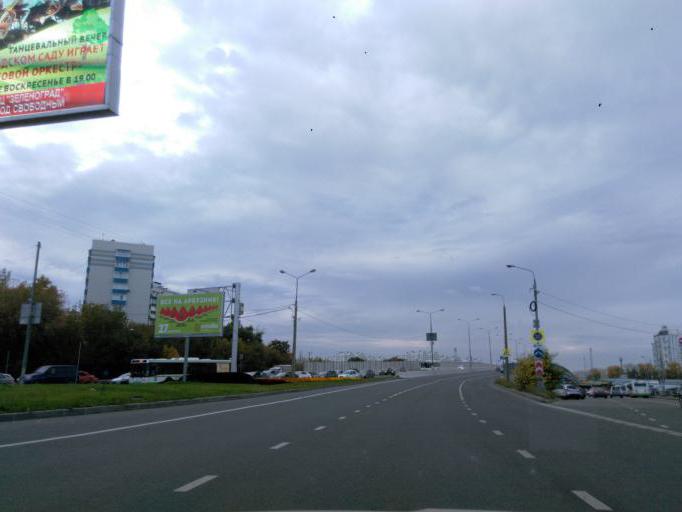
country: RU
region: Moscow
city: Zelenograd
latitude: 55.9827
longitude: 37.1774
